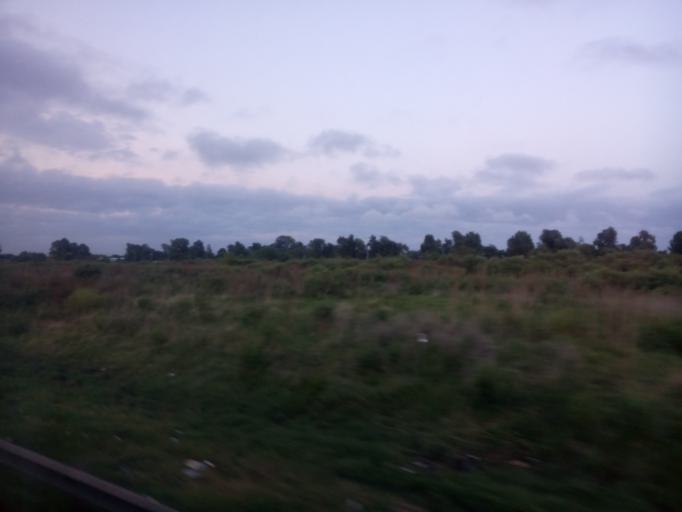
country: AR
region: Buenos Aires
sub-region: Partido de Zarate
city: Zarate
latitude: -34.1190
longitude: -59.0126
